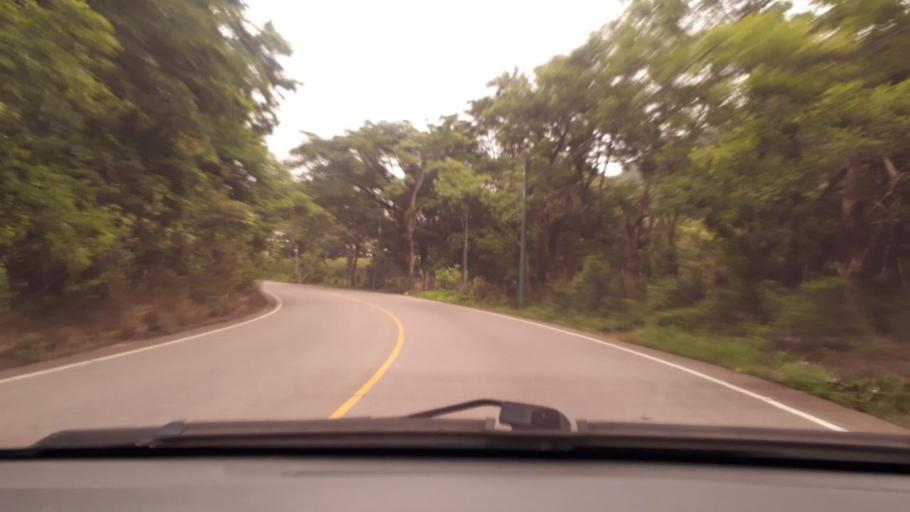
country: GT
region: Chiquimula
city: Concepcion Las Minas
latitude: 14.4720
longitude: -89.4596
